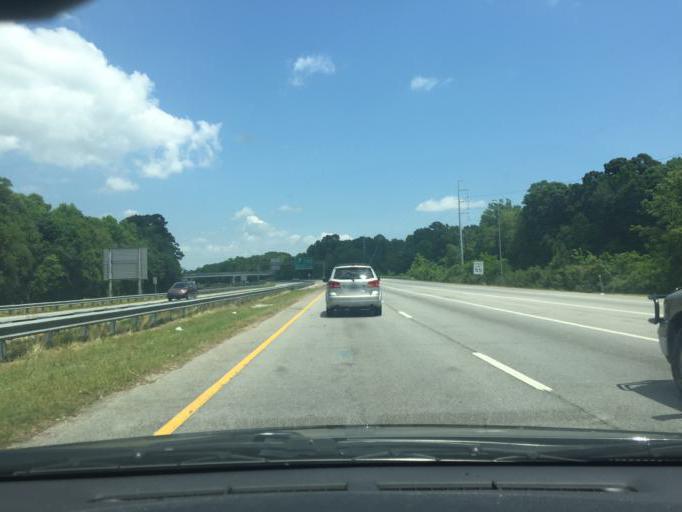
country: US
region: Georgia
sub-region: Chatham County
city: Thunderbolt
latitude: 32.0262
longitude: -81.0863
